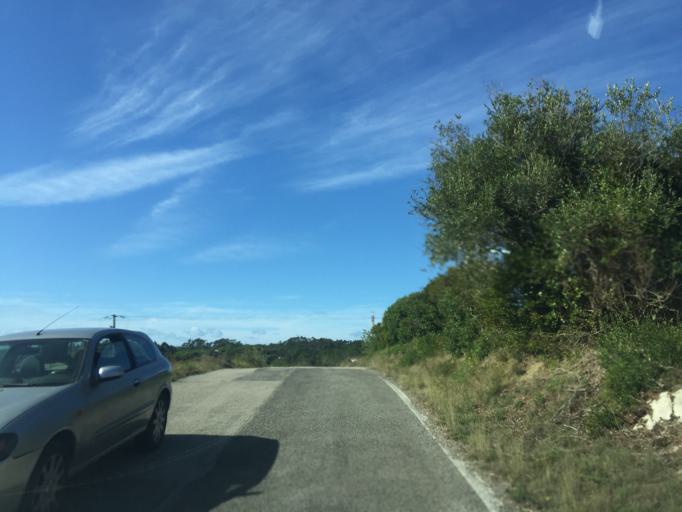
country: PT
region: Coimbra
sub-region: Figueira da Foz
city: Tavarede
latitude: 40.1956
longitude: -8.8554
